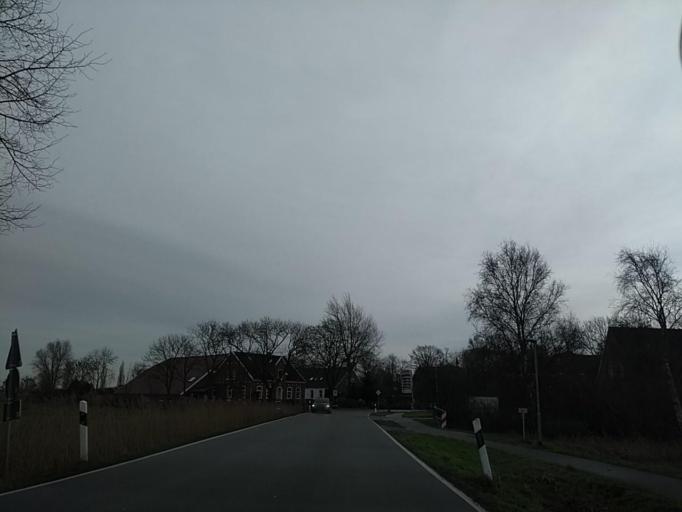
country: DE
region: Lower Saxony
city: Jemgum
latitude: 53.2866
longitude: 7.3701
